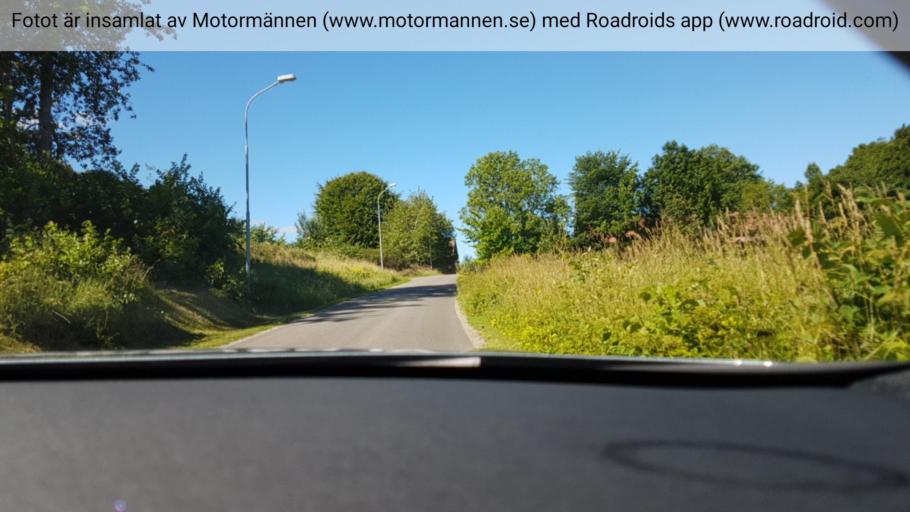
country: SE
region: Vaestra Goetaland
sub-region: Skovde Kommun
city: Skultorp
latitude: 58.2254
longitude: 13.8004
